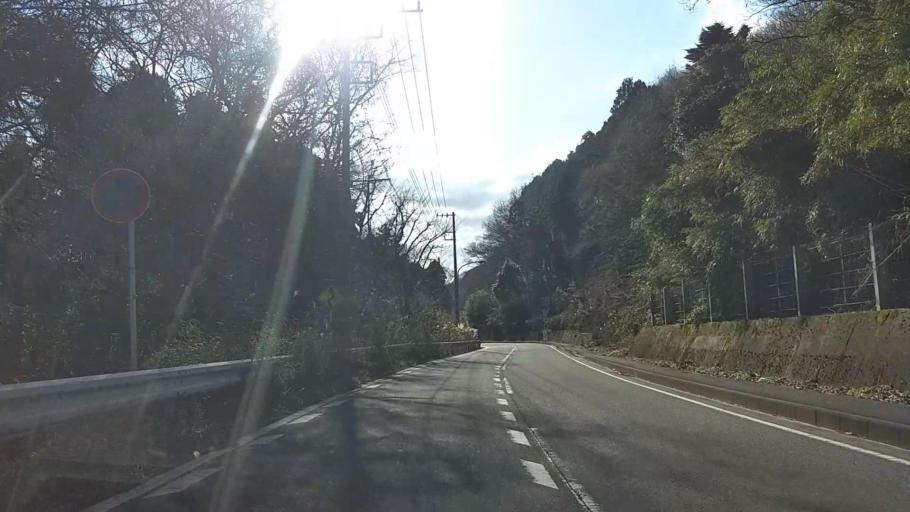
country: JP
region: Kanagawa
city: Atsugi
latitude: 35.4623
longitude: 139.2905
